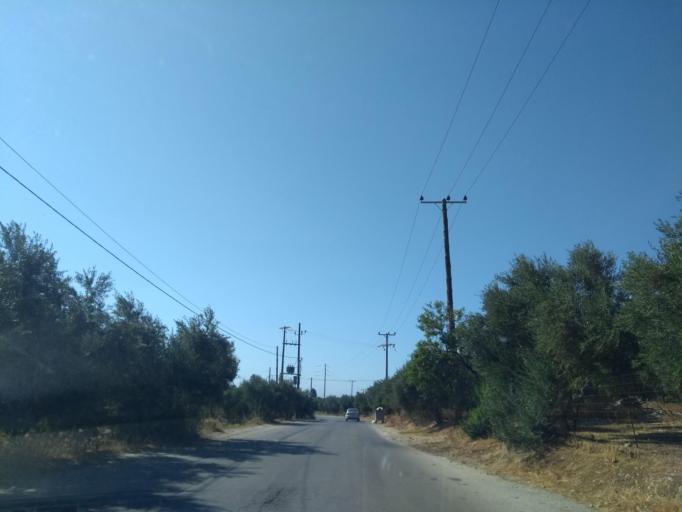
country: GR
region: Crete
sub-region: Nomos Chanias
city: Kissamos
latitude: 35.4996
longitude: 23.7161
